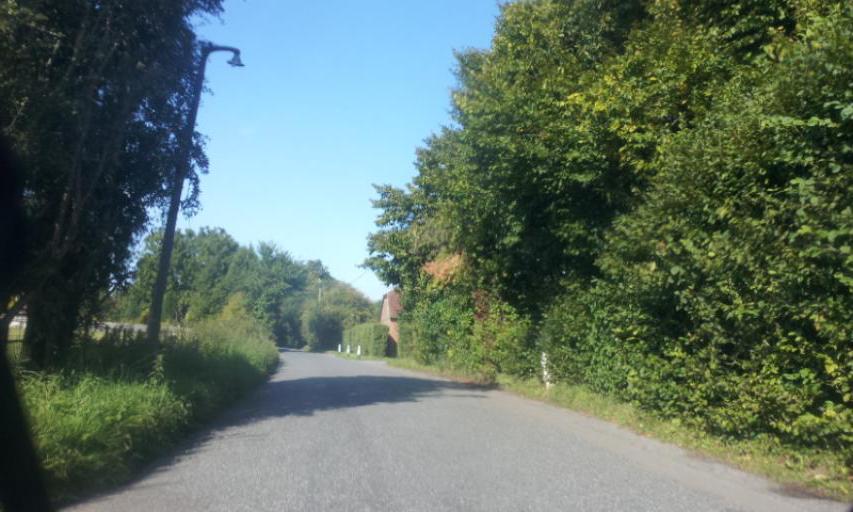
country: GB
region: England
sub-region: Kent
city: Hadlow
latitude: 51.2299
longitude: 0.3321
